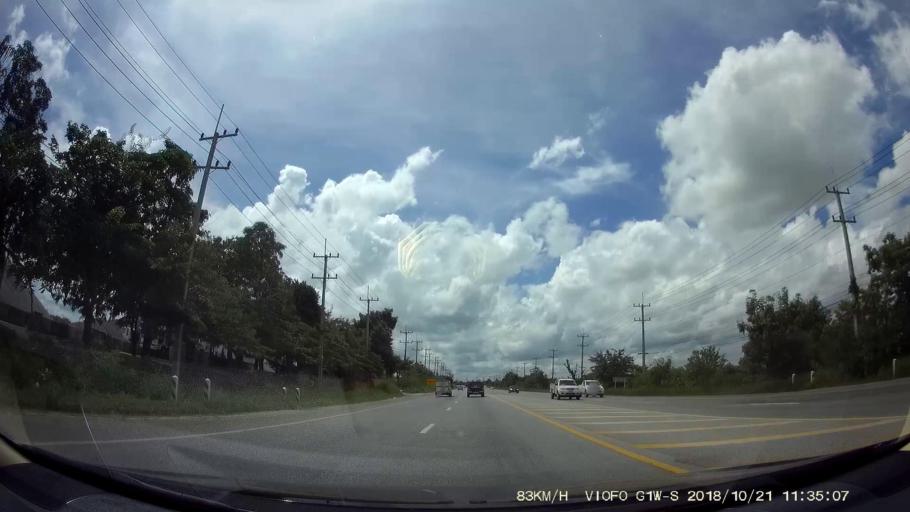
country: TH
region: Chaiyaphum
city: Chaiyaphum
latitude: 15.7248
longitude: 102.0187
